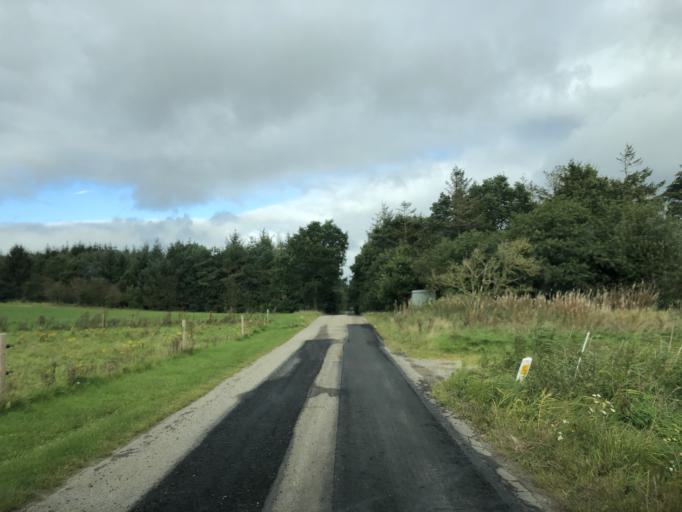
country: DK
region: Central Jutland
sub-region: Holstebro Kommune
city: Ulfborg
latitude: 56.3020
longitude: 8.4384
